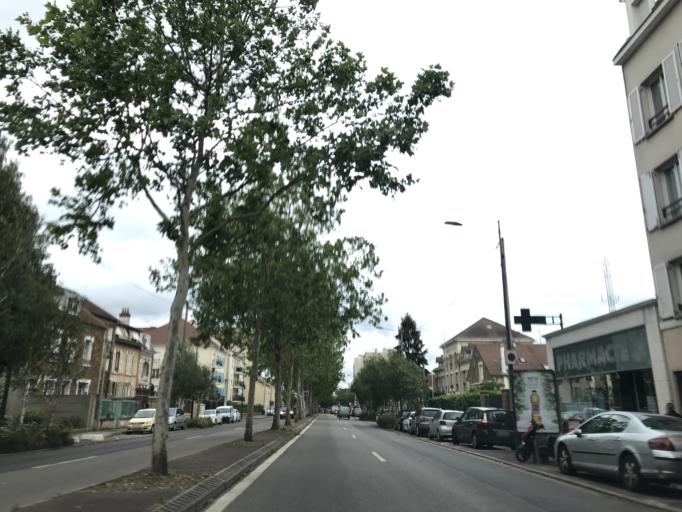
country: FR
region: Ile-de-France
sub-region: Departement des Yvelines
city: Mantes-la-Jolie
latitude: 48.9930
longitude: 1.7007
